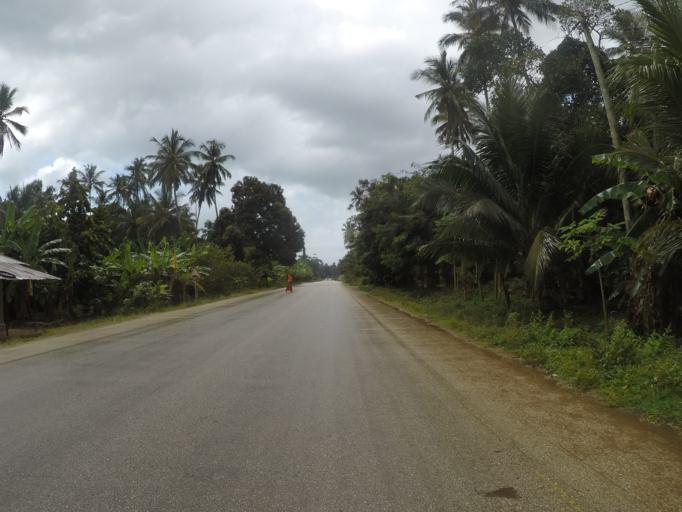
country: TZ
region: Zanzibar North
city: Mkokotoni
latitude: -5.9733
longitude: 39.1964
